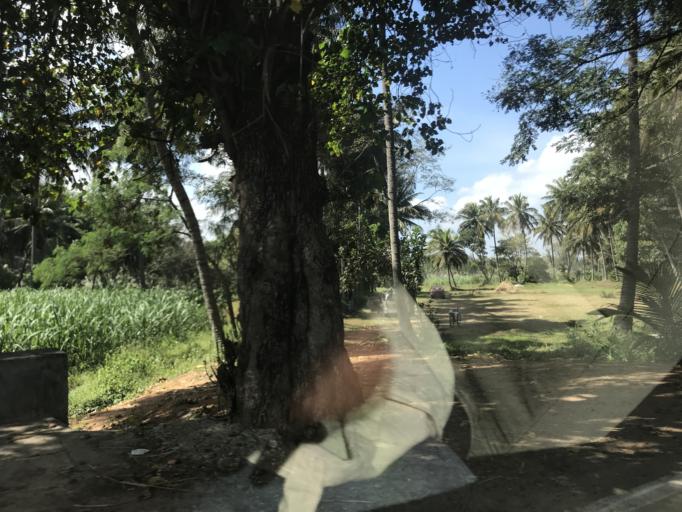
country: IN
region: Karnataka
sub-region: Mandya
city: Shrirangapattana
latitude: 12.4200
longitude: 76.6583
